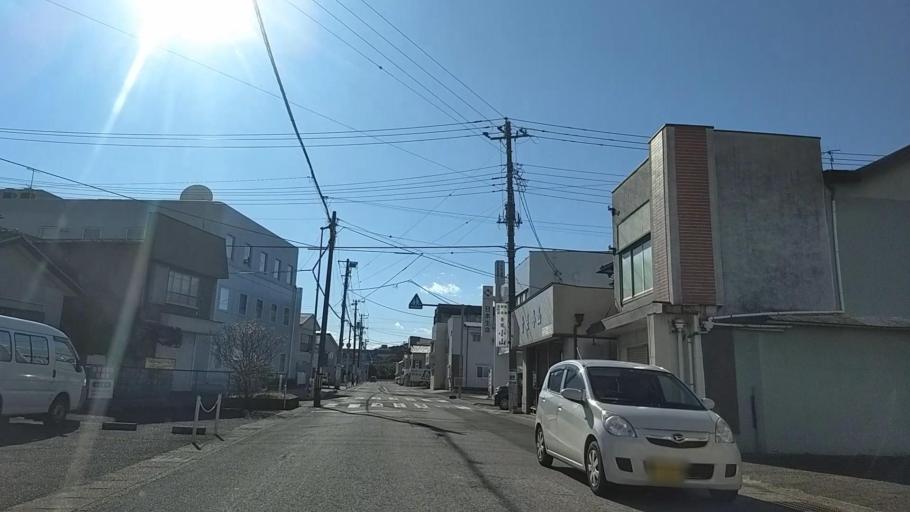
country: JP
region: Chiba
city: Tateyama
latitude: 34.9879
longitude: 139.8624
